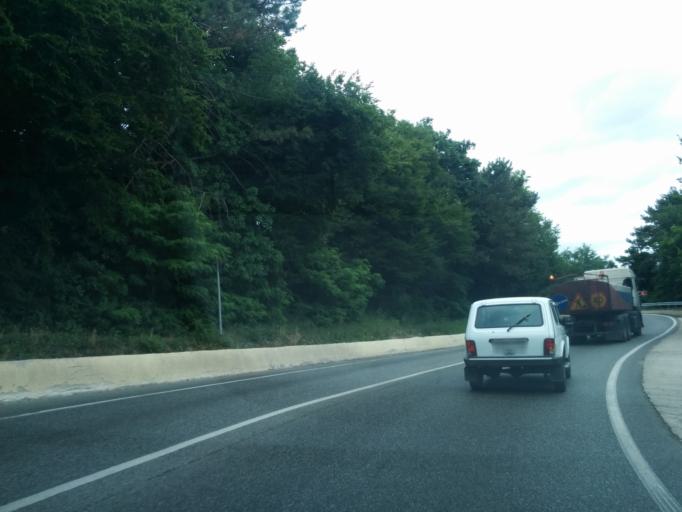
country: RU
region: Krasnodarskiy
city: Agoy
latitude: 44.1228
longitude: 39.0491
